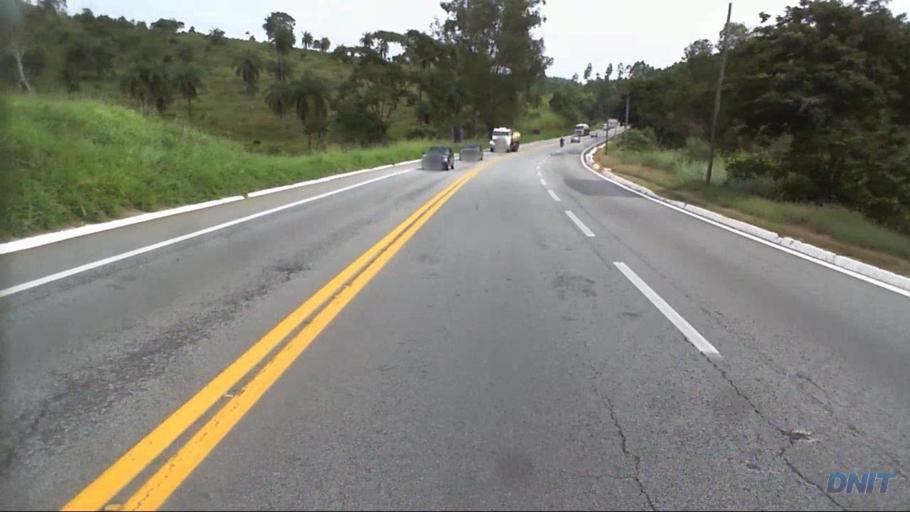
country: BR
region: Minas Gerais
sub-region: Caete
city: Caete
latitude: -19.7257
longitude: -43.5872
